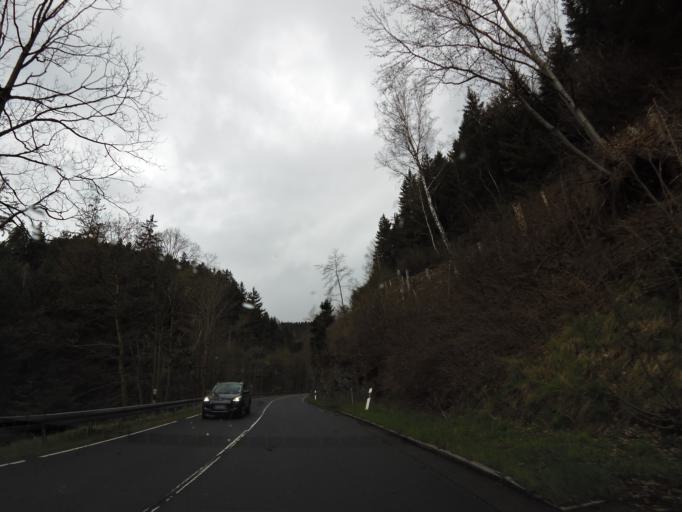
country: DE
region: Lower Saxony
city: Schulenberg im Oberharz
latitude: 51.8636
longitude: 10.4752
